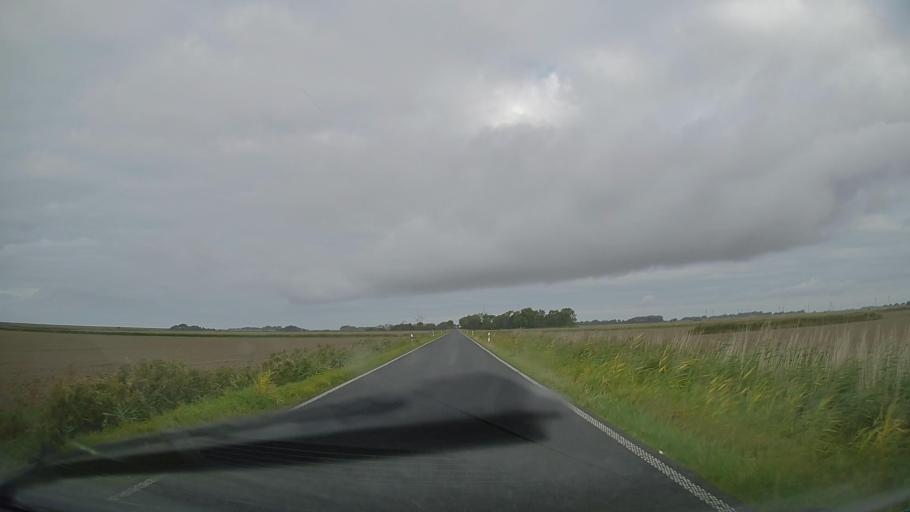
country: DE
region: Schleswig-Holstein
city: Galmsbull
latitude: 54.7492
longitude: 8.7322
